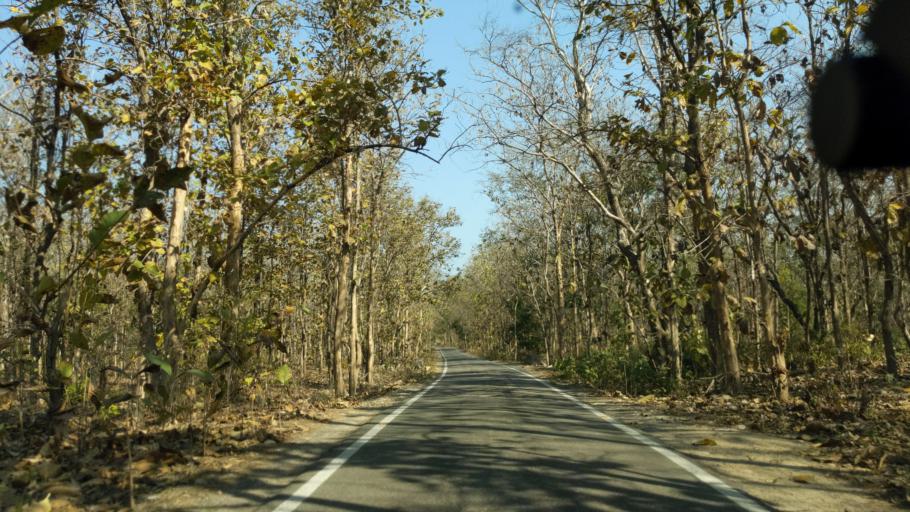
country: IN
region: Uttarakhand
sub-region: Naini Tal
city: Ramnagar
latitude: 29.4298
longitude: 79.1407
